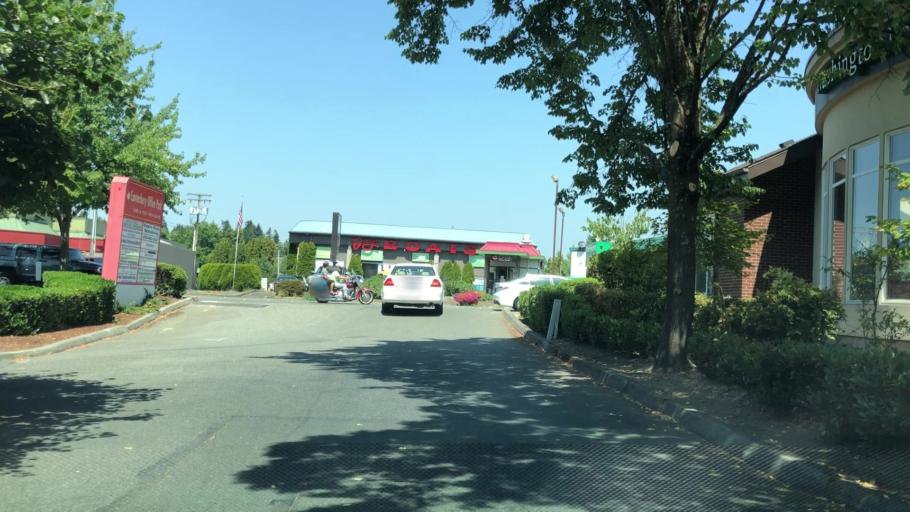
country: US
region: Washington
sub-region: King County
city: Woodinville
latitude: 47.7540
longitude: -122.1601
